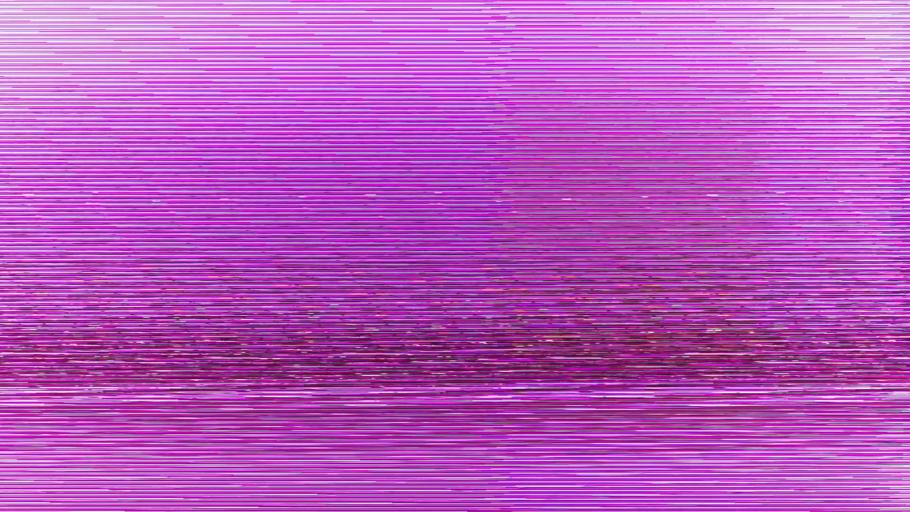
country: US
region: Michigan
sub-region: Livingston County
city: Brighton
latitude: 42.5371
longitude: -83.7844
